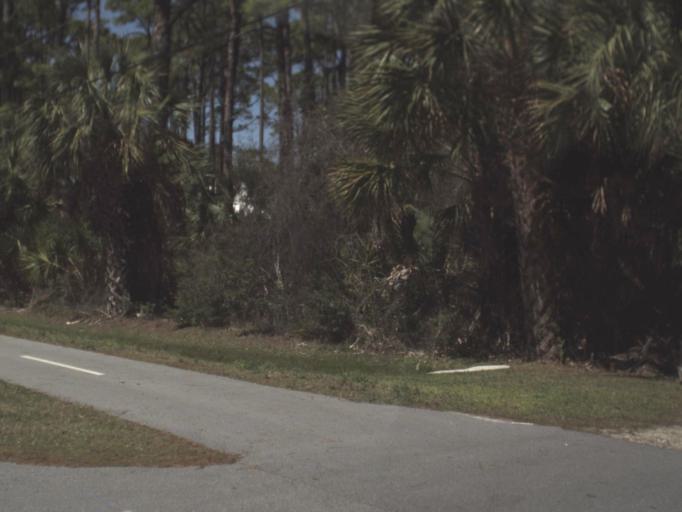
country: US
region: Florida
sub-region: Gulf County
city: Port Saint Joe
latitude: 29.6846
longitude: -85.3168
